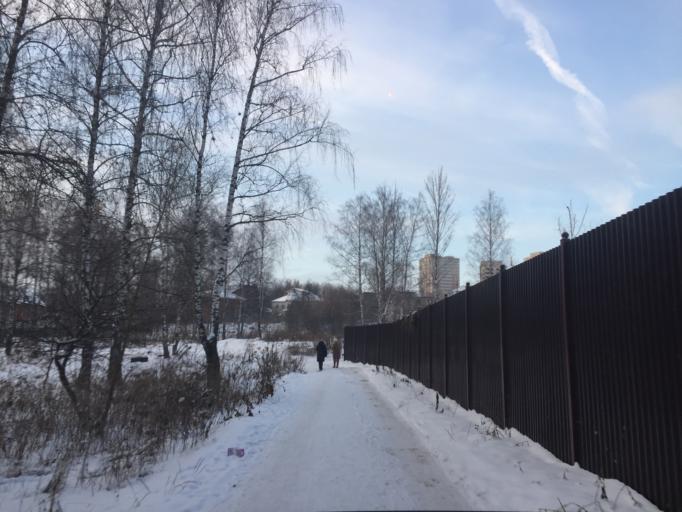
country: RU
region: Tula
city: Tula
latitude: 54.2020
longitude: 37.6650
